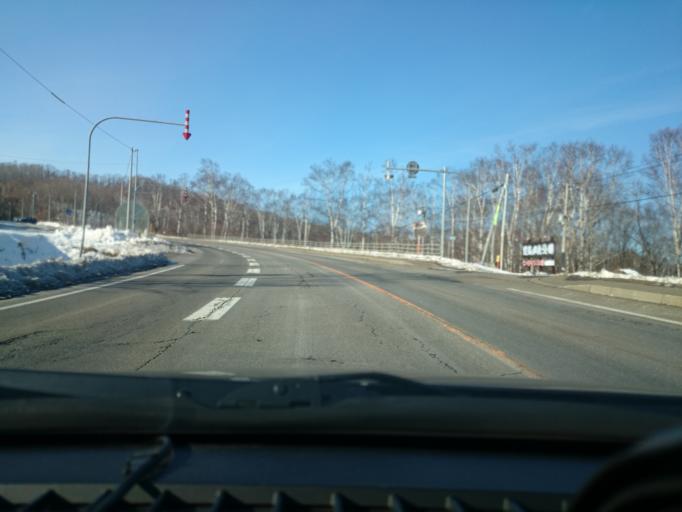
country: JP
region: Hokkaido
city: Otofuke
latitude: 43.2385
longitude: 143.5370
